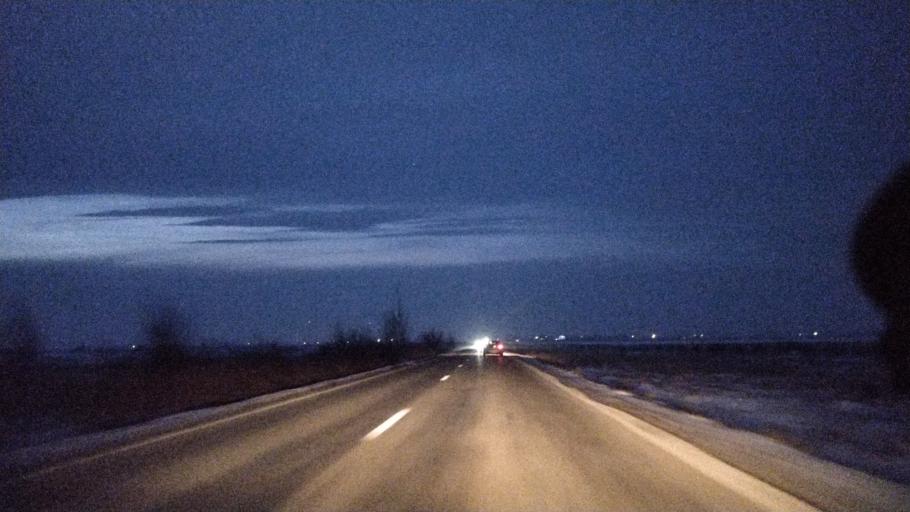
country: RO
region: Vrancea
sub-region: Comuna Milcovul
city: Milcovul
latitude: 45.6716
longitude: 27.2588
